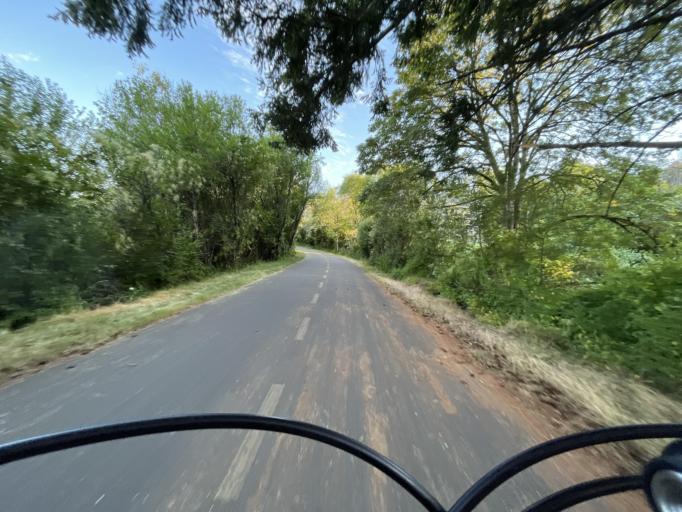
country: CA
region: British Columbia
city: Colwood
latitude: 48.4525
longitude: -123.4705
